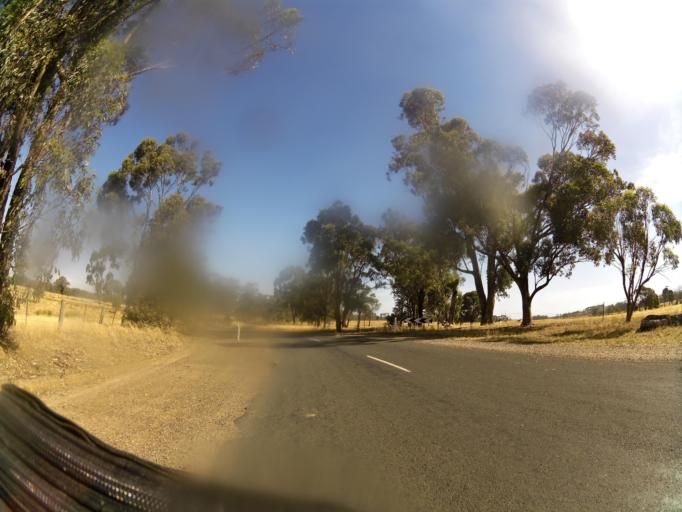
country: AU
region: Victoria
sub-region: Campaspe
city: Kyabram
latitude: -36.8952
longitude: 145.1068
